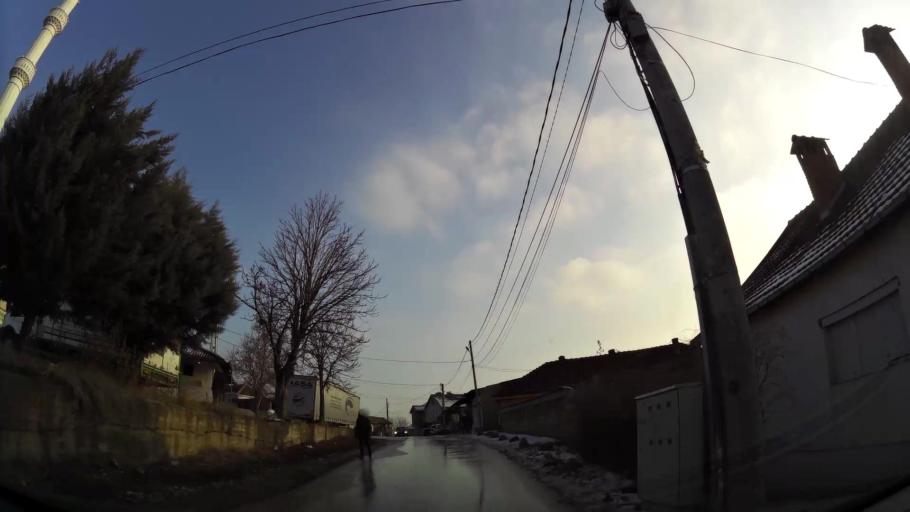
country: MK
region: Aracinovo
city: Arachinovo
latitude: 42.0247
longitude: 21.5653
